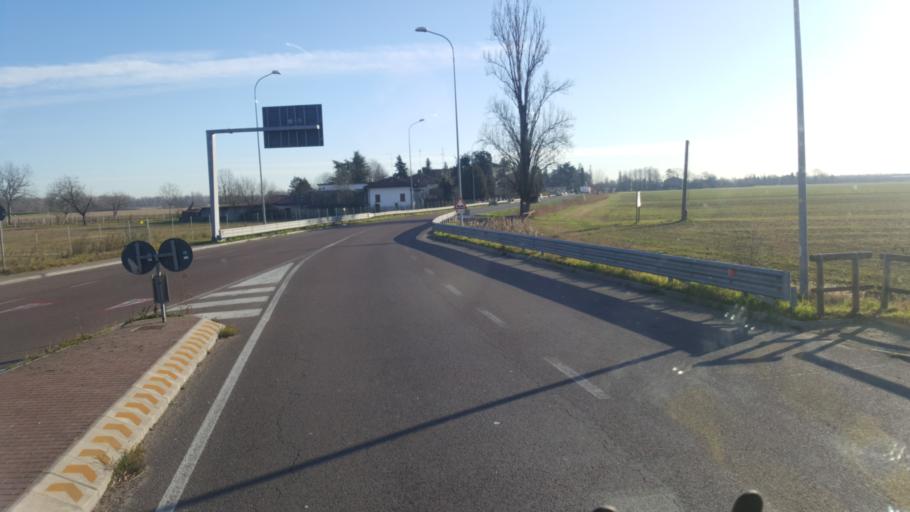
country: IT
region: Emilia-Romagna
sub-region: Provincia di Reggio Emilia
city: Rubiera
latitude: 44.6509
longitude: 10.8096
